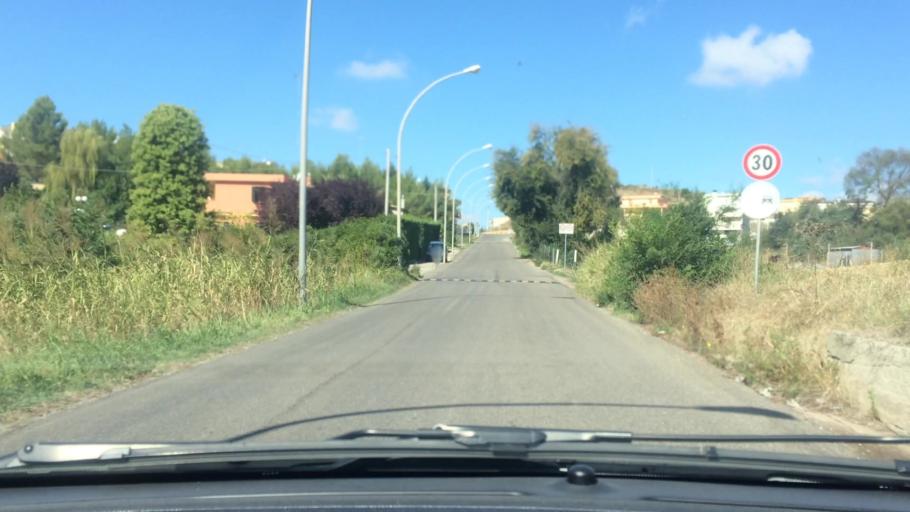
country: IT
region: Basilicate
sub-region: Provincia di Matera
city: Montescaglioso
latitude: 40.5431
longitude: 16.6709
